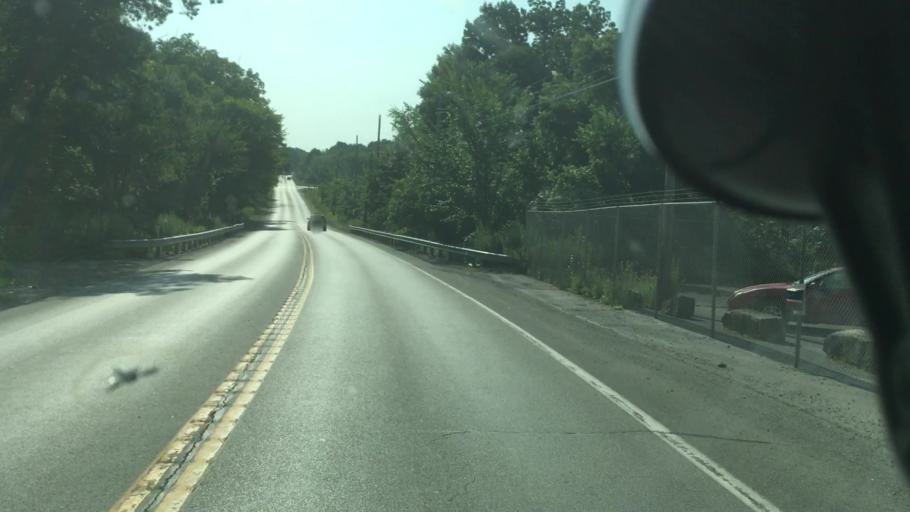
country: US
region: Ohio
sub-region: Mahoning County
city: Lowellville
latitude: 41.0215
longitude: -80.5114
